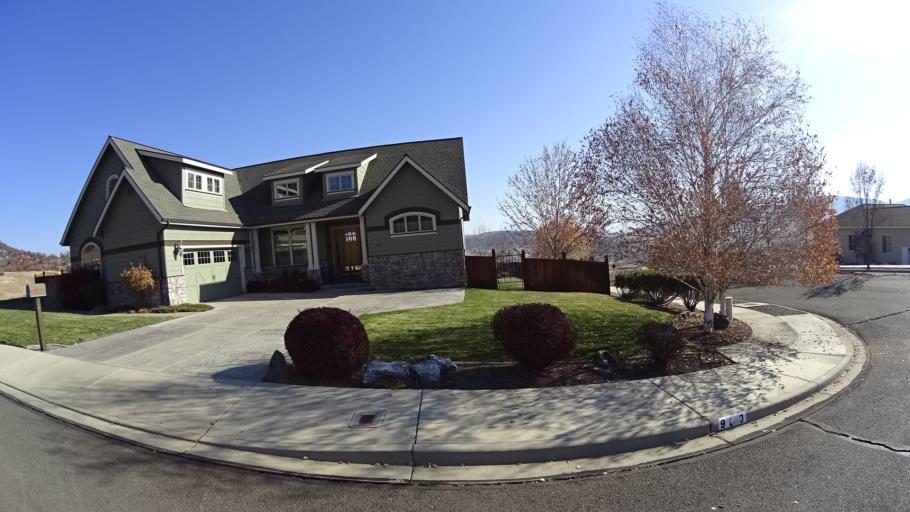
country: US
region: California
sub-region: Siskiyou County
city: Yreka
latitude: 41.7457
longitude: -122.6421
